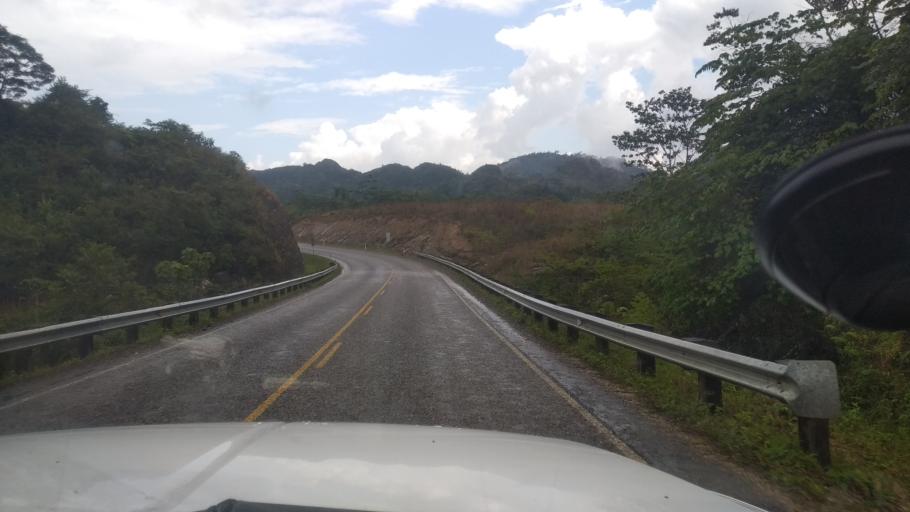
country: GT
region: Peten
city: San Luis
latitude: 16.1844
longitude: -89.2048
